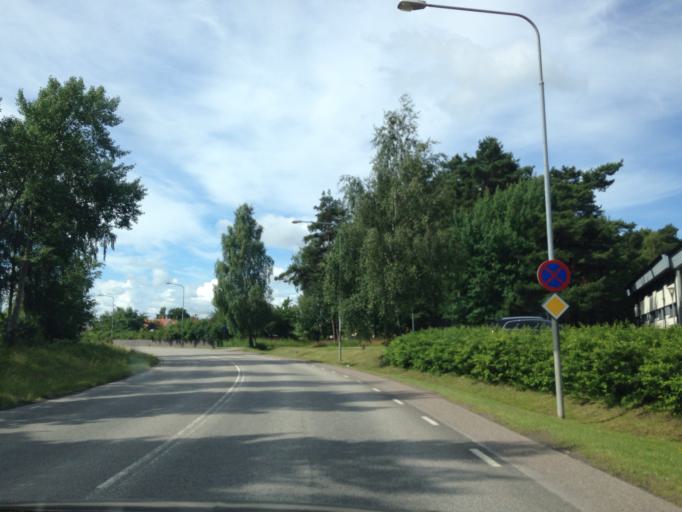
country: SE
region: Kalmar
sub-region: Kalmar Kommun
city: Kalmar
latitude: 56.6775
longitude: 16.3575
